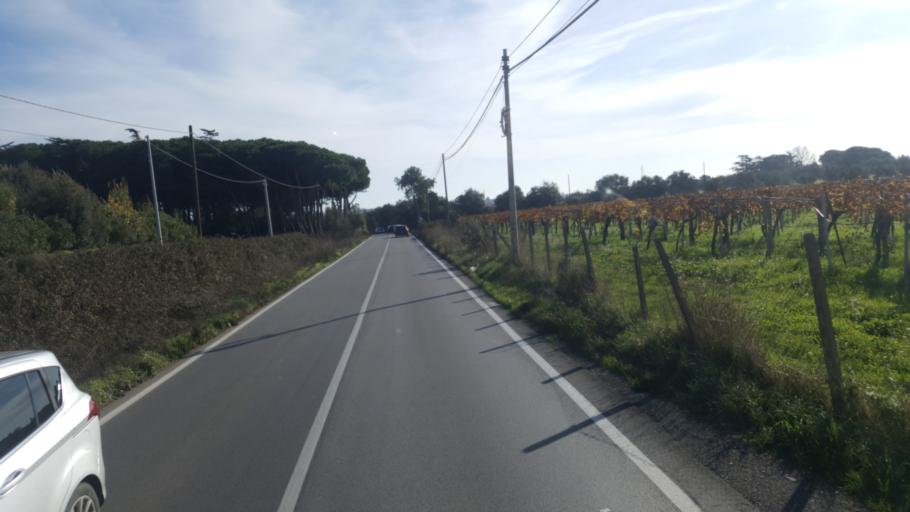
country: IT
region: Latium
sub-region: Citta metropolitana di Roma Capitale
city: Mantiglia di Ardea
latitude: 41.6855
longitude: 12.6113
